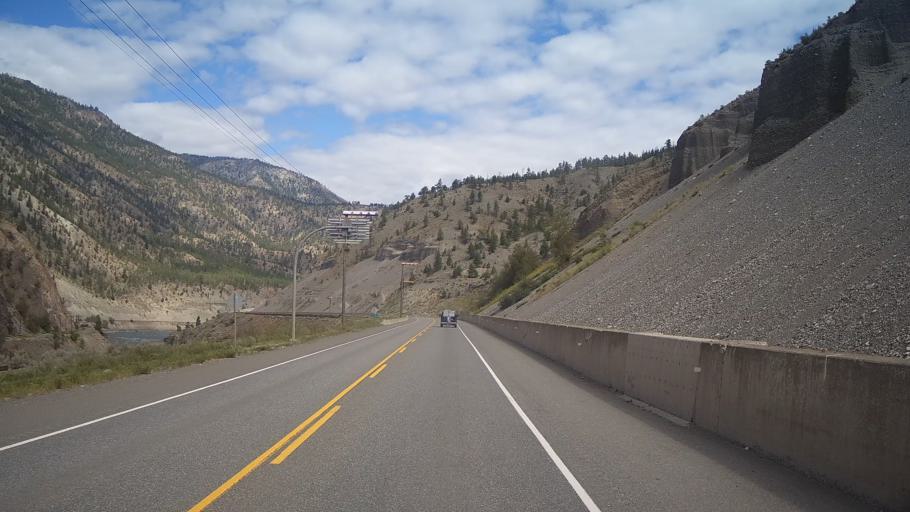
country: CA
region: British Columbia
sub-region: Thompson-Nicola Regional District
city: Ashcroft
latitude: 50.2702
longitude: -121.4014
